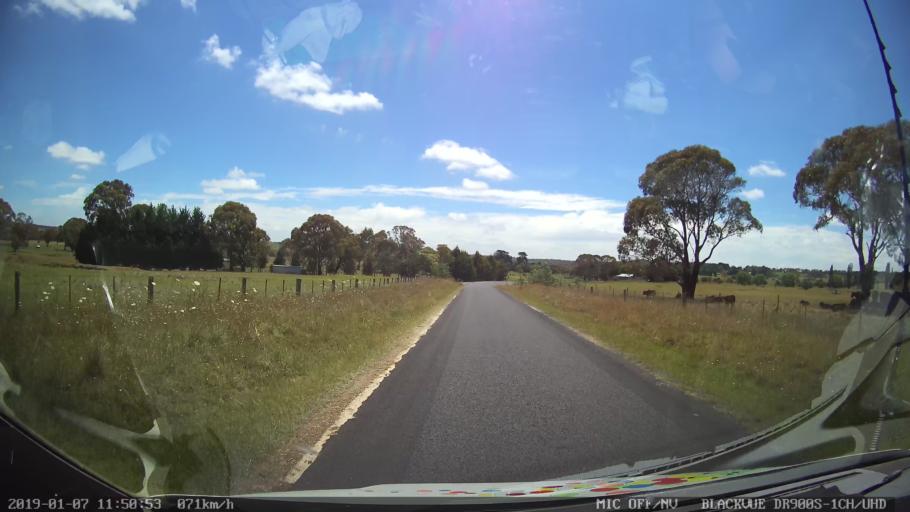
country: AU
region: New South Wales
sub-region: Guyra
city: Guyra
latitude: -30.3102
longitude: 151.6406
